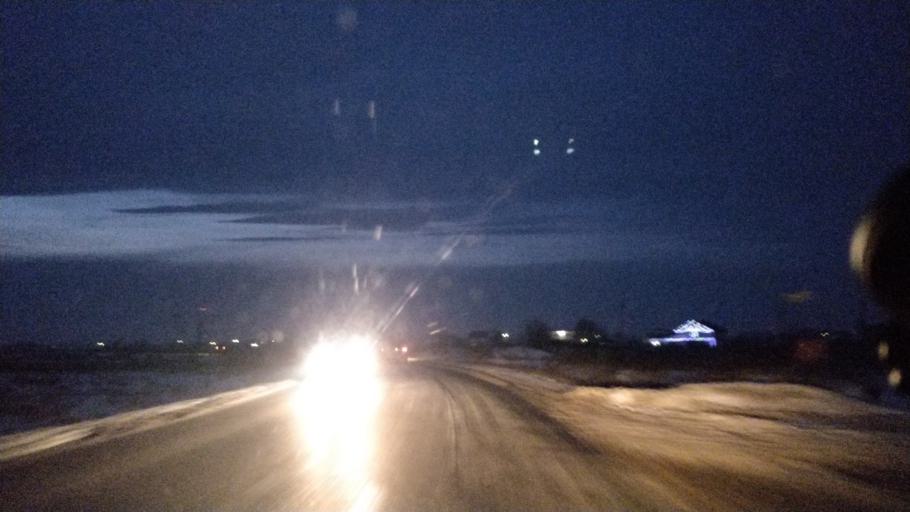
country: RO
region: Vrancea
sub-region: Comuna Milcovul
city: Milcovul
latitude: 45.6767
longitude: 27.2516
